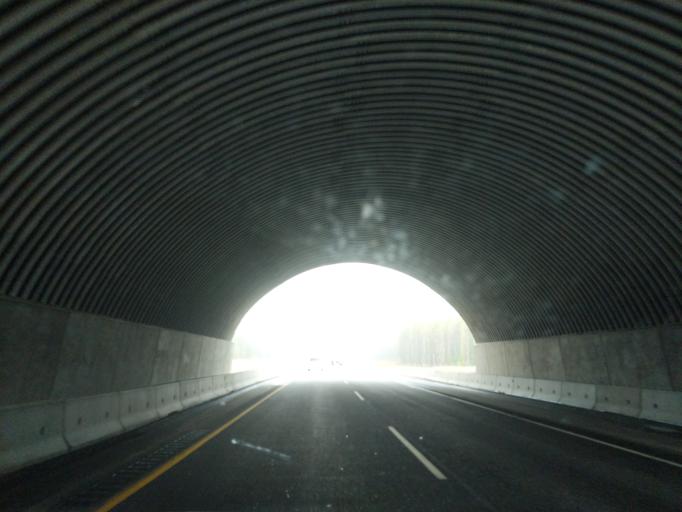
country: CA
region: Alberta
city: Lake Louise
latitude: 51.3008
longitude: -116.0130
